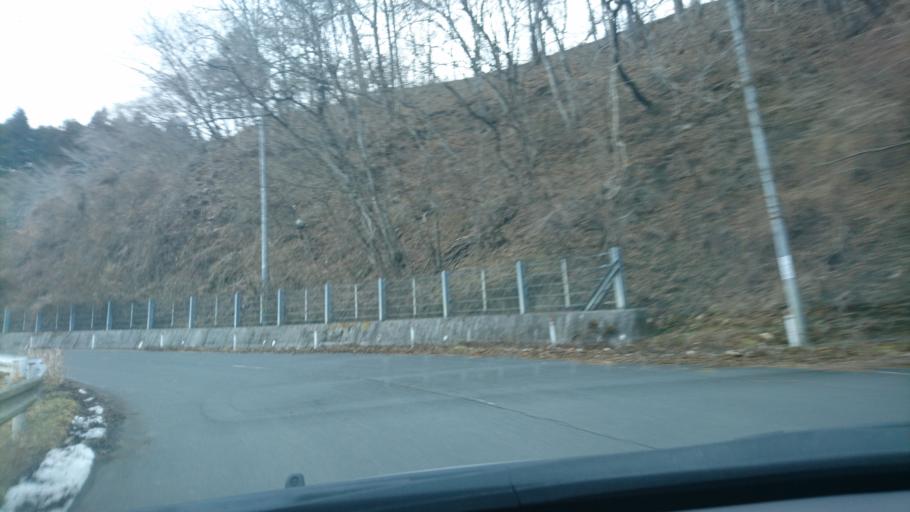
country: JP
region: Iwate
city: Ofunato
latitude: 38.9137
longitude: 141.5126
